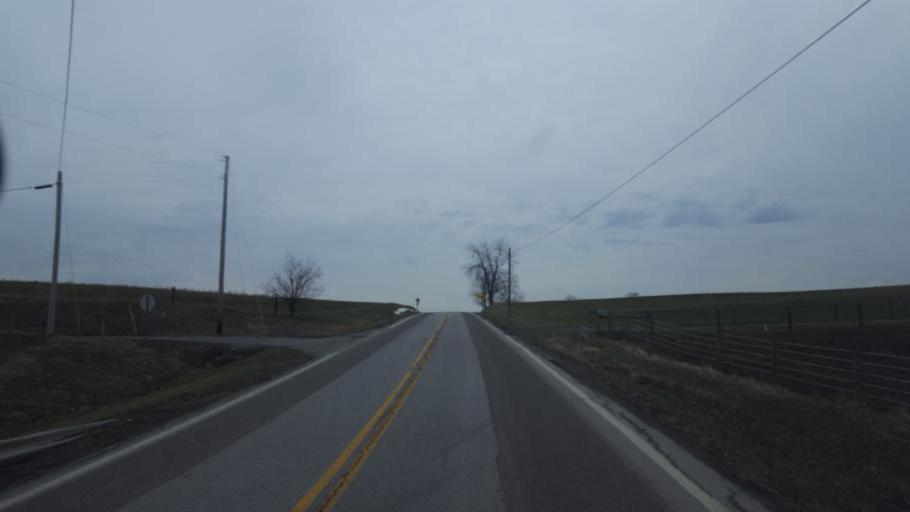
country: US
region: Ohio
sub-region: Tuscarawas County
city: Sugarcreek
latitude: 40.4957
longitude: -81.7704
